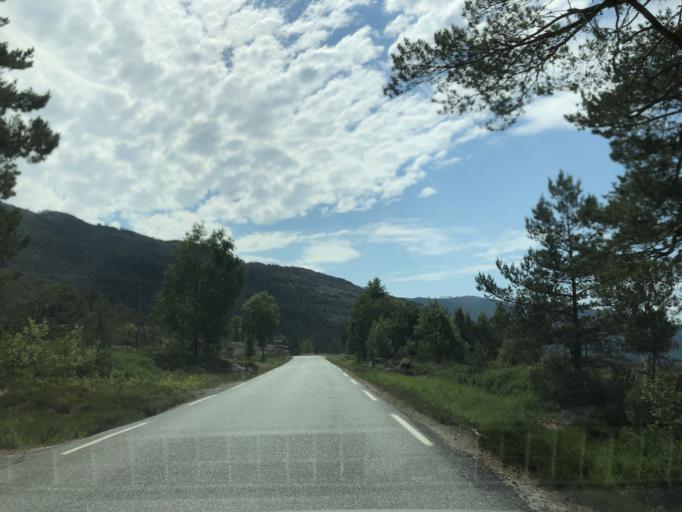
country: NO
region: Hordaland
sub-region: Jondal
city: Jondal
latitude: 60.3300
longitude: 6.3390
